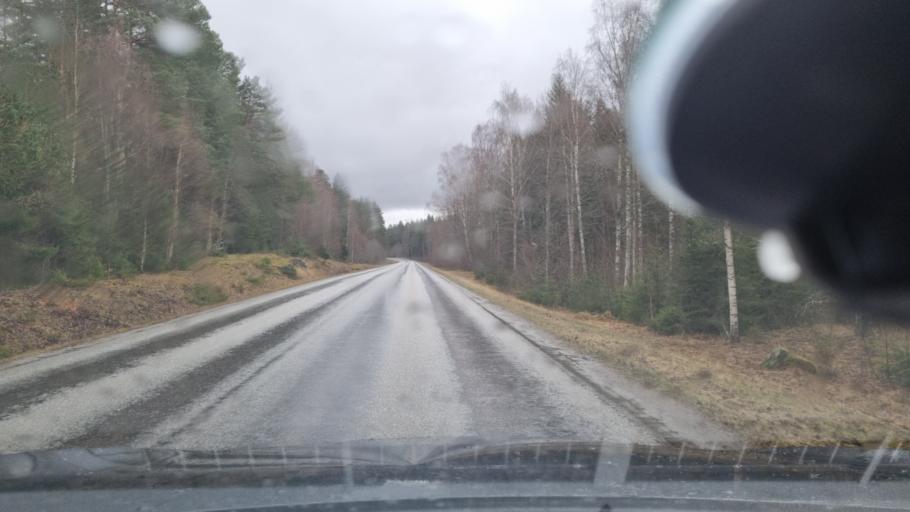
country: SE
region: Stockholm
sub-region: Upplands-Bro Kommun
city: Kungsaengen
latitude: 59.5447
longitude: 17.7392
